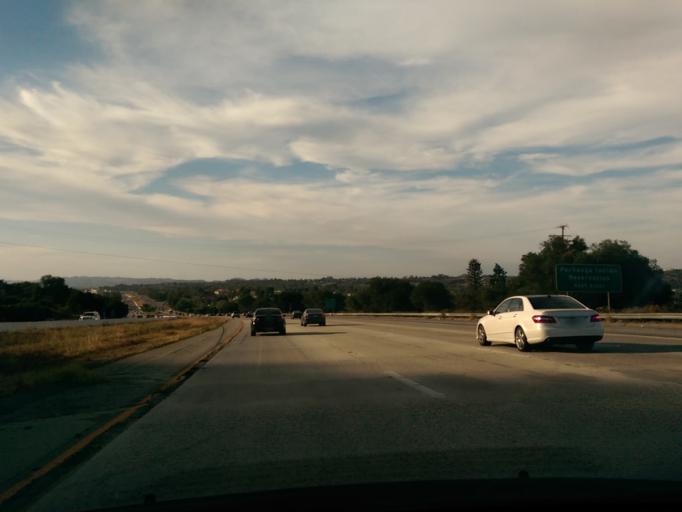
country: US
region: California
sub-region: Riverside County
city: Temecula
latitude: 33.4666
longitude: -117.1361
